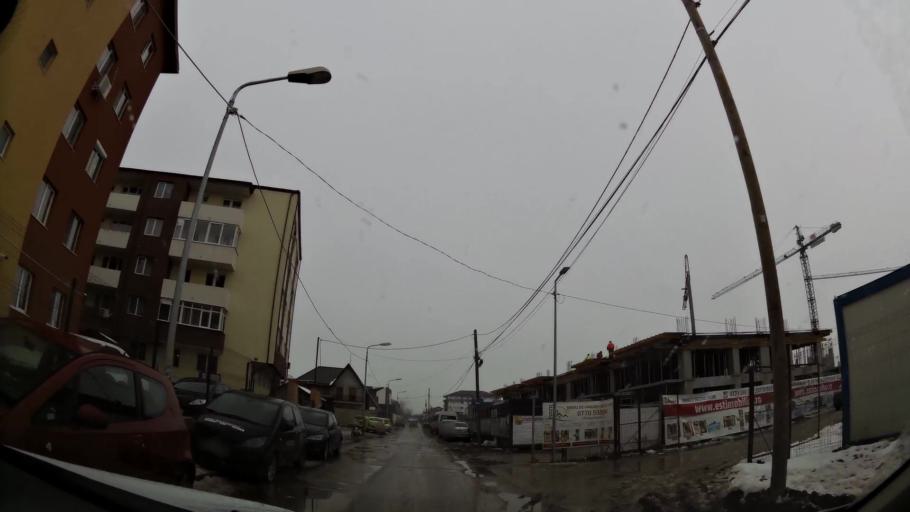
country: RO
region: Ilfov
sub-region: Comuna Glina
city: Catelu
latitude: 44.4157
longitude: 26.1896
